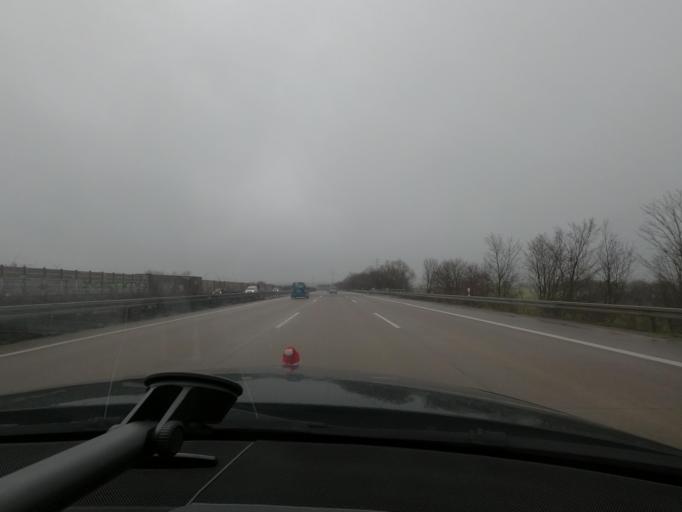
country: DE
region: Lower Saxony
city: Sehnde
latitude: 52.2838
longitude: 9.9056
